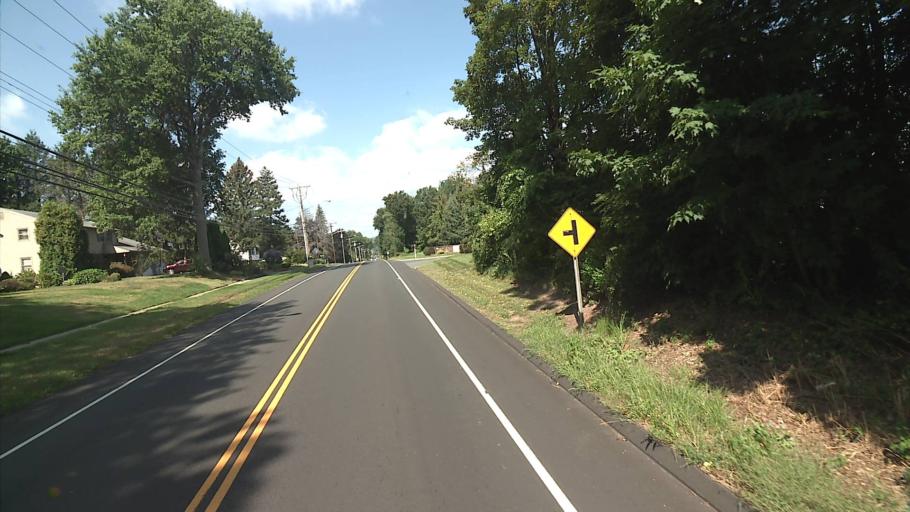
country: US
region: Connecticut
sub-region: Hartford County
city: Blue Hills
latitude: 41.8013
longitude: -72.7355
